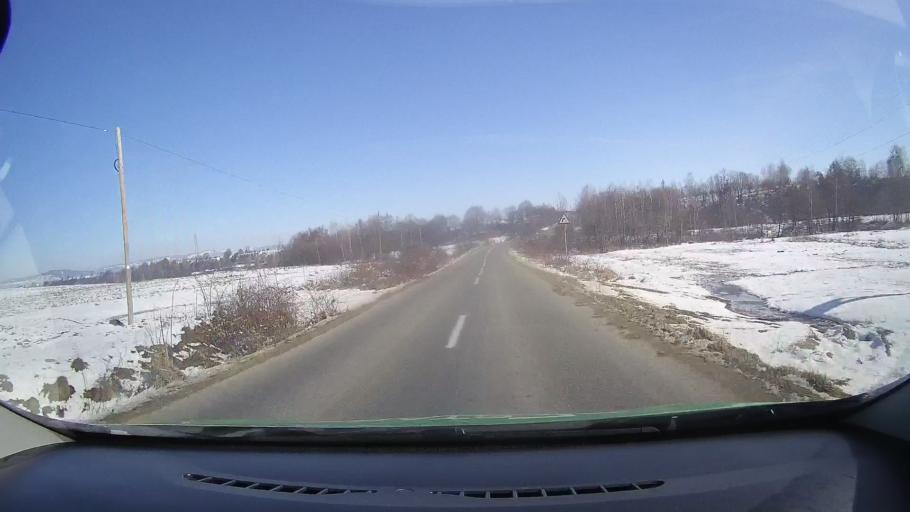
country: RO
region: Brasov
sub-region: Oras Victoria
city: Victoria
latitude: 45.7298
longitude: 24.7117
